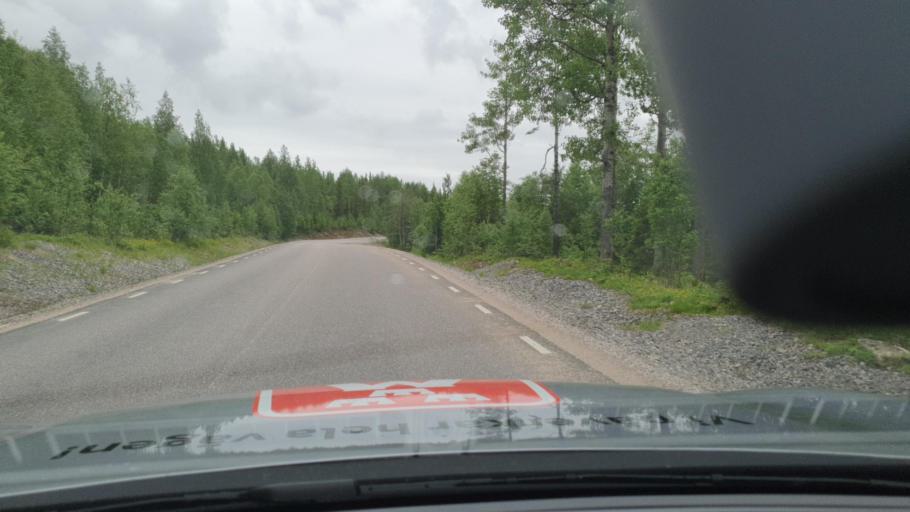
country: SE
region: Norrbotten
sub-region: Overtornea Kommun
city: OEvertornea
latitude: 66.5229
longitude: 23.3736
